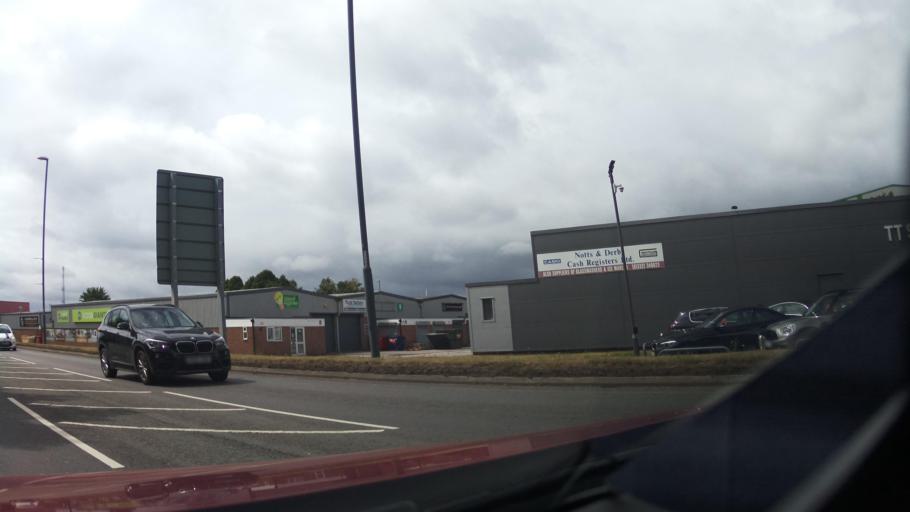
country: GB
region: England
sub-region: Derby
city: Derby
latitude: 52.9323
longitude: -1.4649
